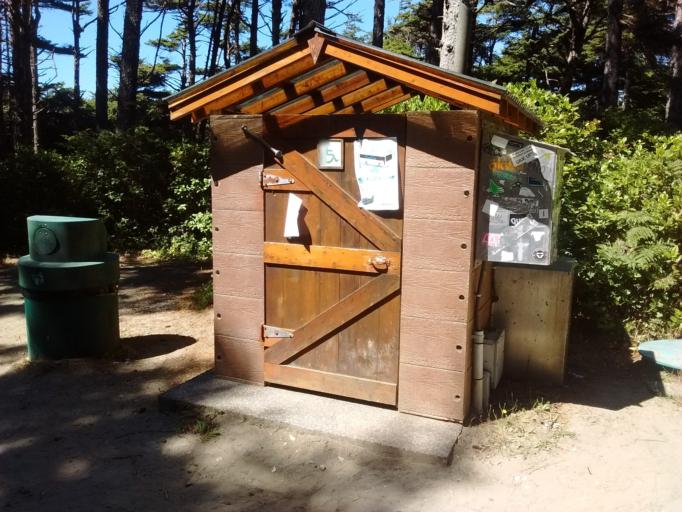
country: CA
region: British Columbia
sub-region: Regional District of Alberni-Clayoquot
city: Tofino
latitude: 49.1008
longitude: -125.8718
